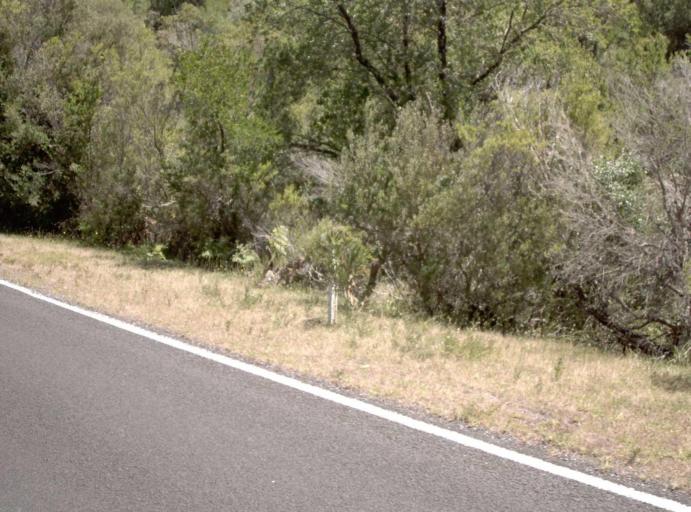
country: AU
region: Victoria
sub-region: Latrobe
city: Morwell
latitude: -38.8837
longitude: 146.2586
